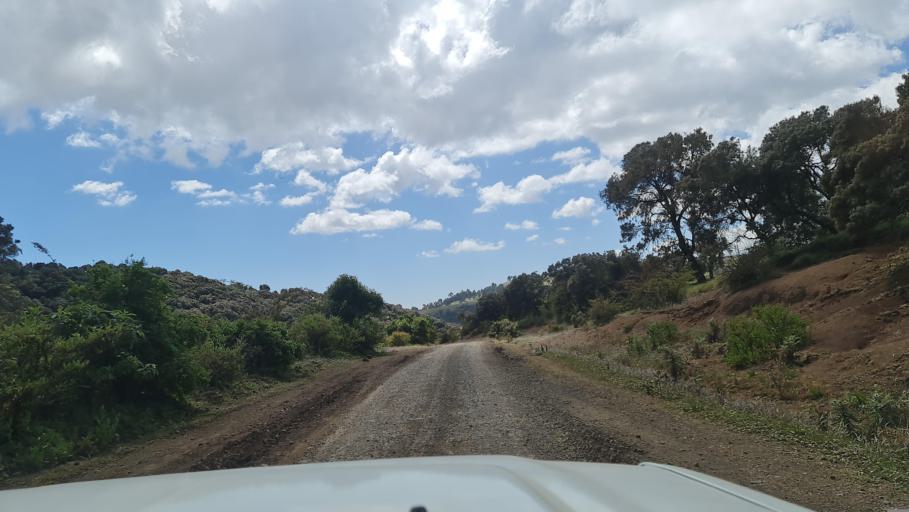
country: ET
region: Amhara
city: Debark'
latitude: 13.2082
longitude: 37.9957
